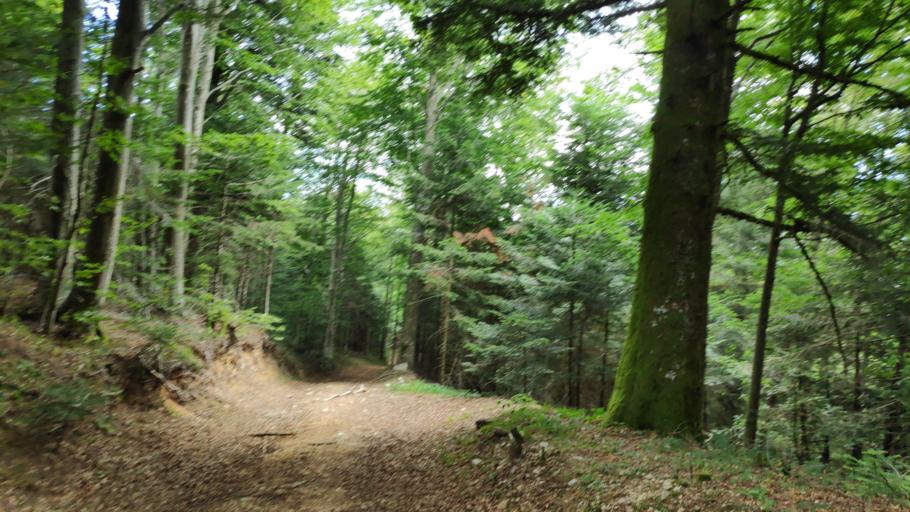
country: IT
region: Calabria
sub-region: Provincia di Vibo-Valentia
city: Serra San Bruno
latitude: 38.5443
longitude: 16.3646
